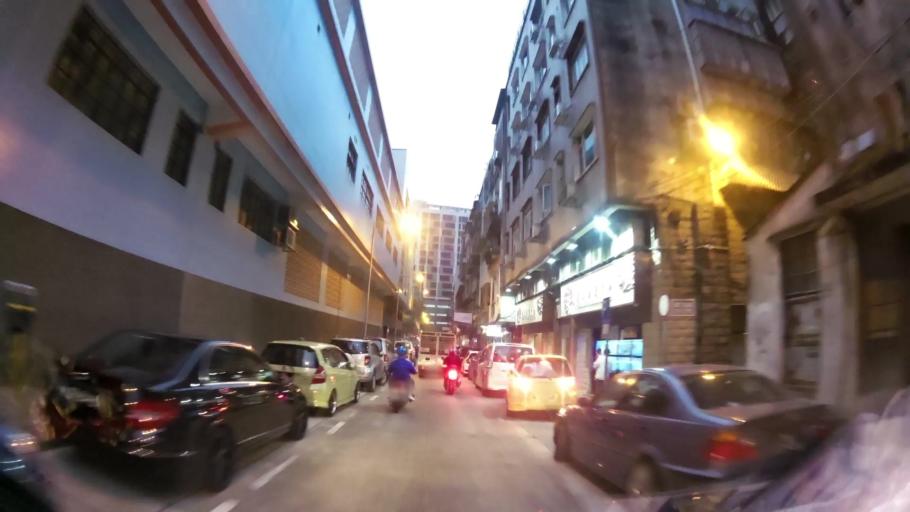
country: MO
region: Macau
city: Macau
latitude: 22.2063
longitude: 113.5462
